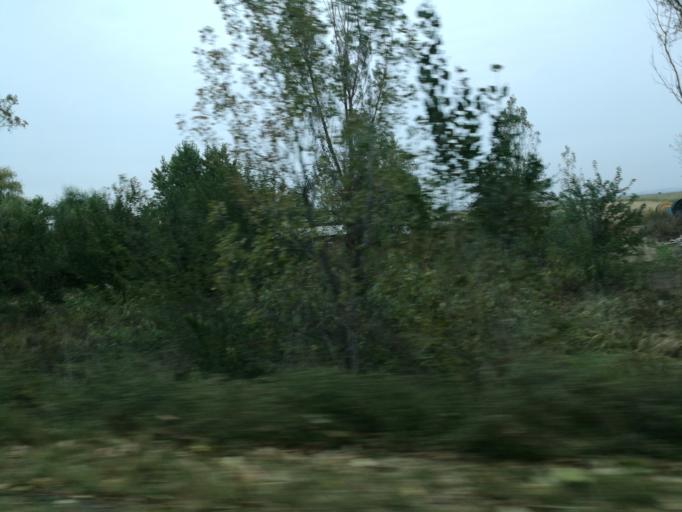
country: RO
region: Braila
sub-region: Municipiul Braila
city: Braila
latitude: 45.2615
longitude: 28.0588
